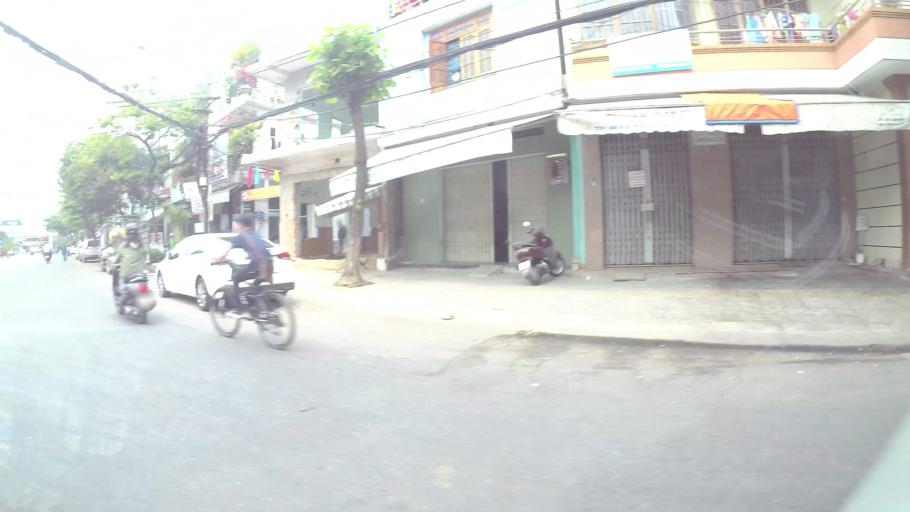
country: VN
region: Da Nang
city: Da Nang
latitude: 16.0566
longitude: 108.2088
